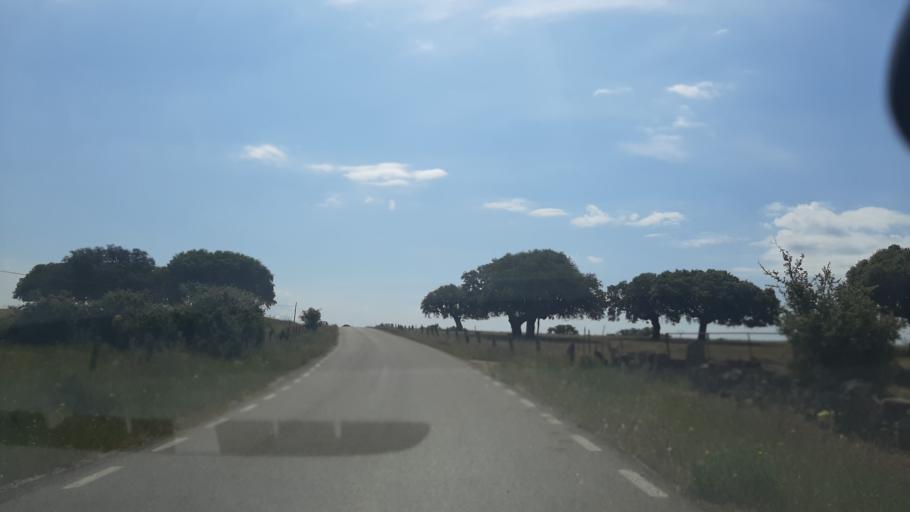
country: ES
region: Castille and Leon
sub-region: Provincia de Salamanca
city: Gallegos de Arganan
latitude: 40.6442
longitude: -6.7446
